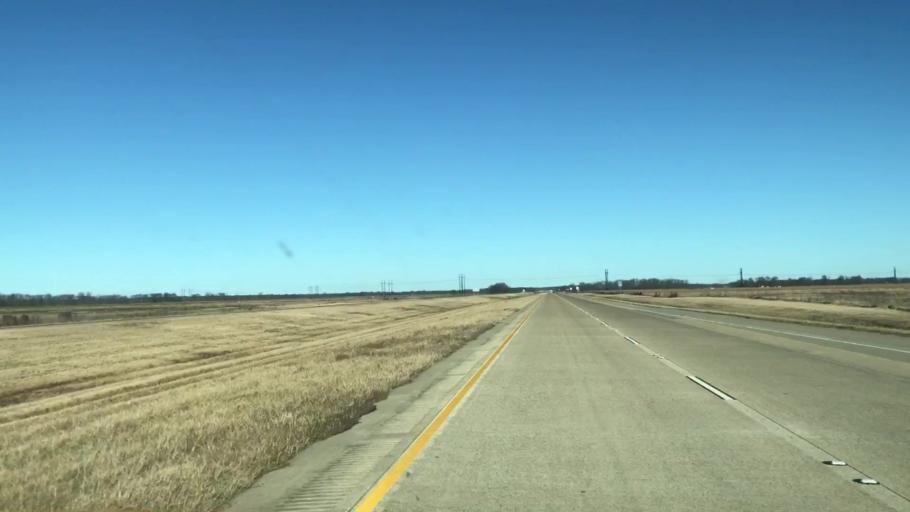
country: US
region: Louisiana
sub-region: Caddo Parish
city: Oil City
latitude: 32.7092
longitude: -93.8642
